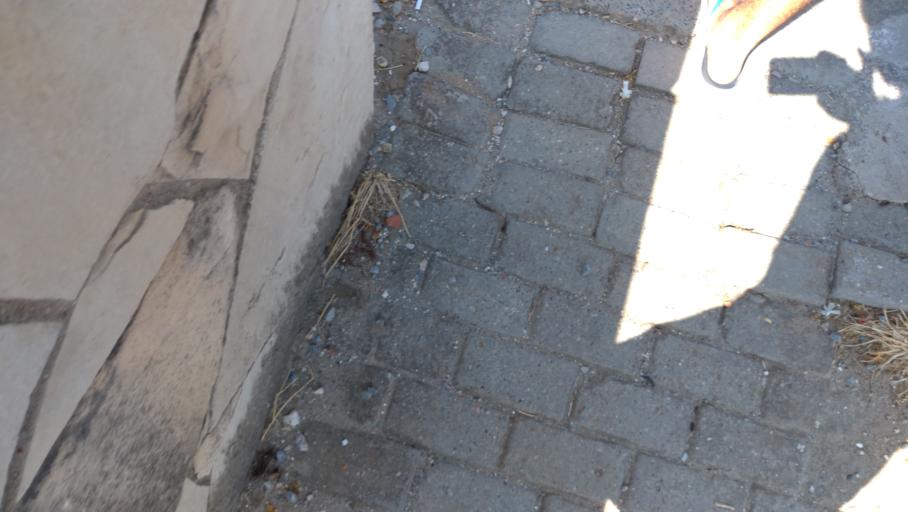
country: TR
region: Izmir
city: Urla
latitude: 38.3282
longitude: 26.7620
